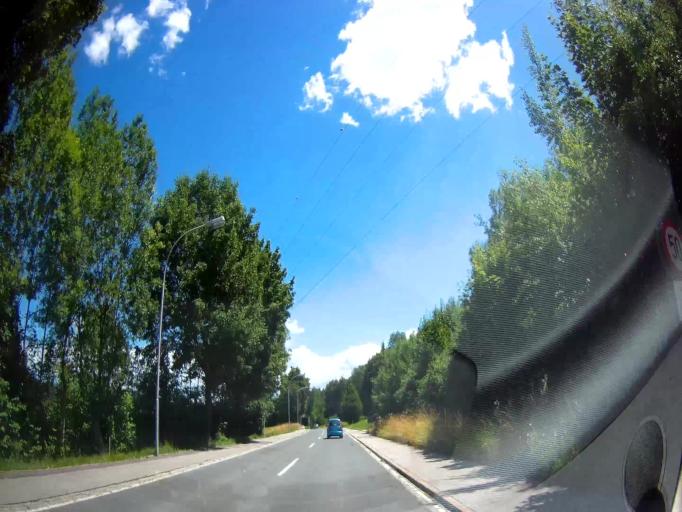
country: AT
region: Carinthia
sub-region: Politischer Bezirk Sankt Veit an der Glan
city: Sankt Veit an der Glan
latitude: 46.7608
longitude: 14.3676
